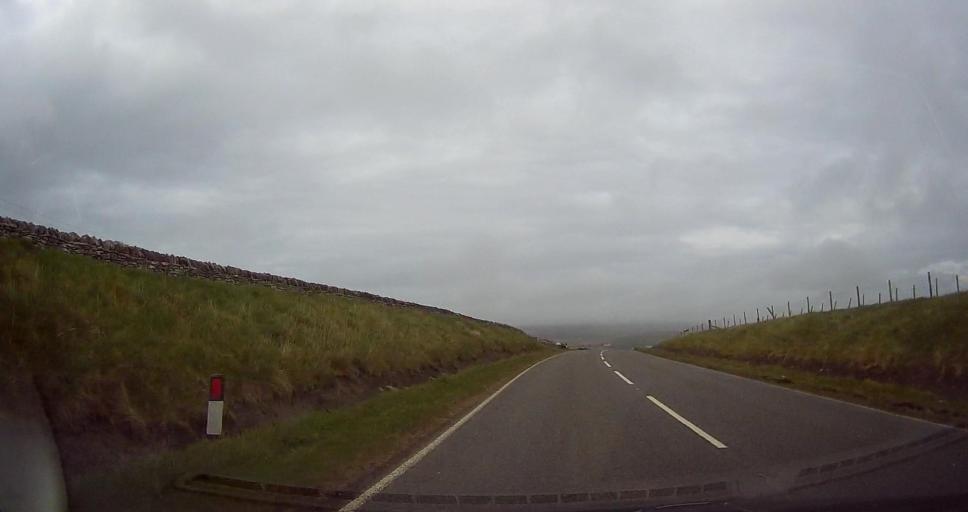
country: GB
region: Scotland
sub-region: Shetland Islands
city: Sandwick
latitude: 59.9120
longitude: -1.3019
